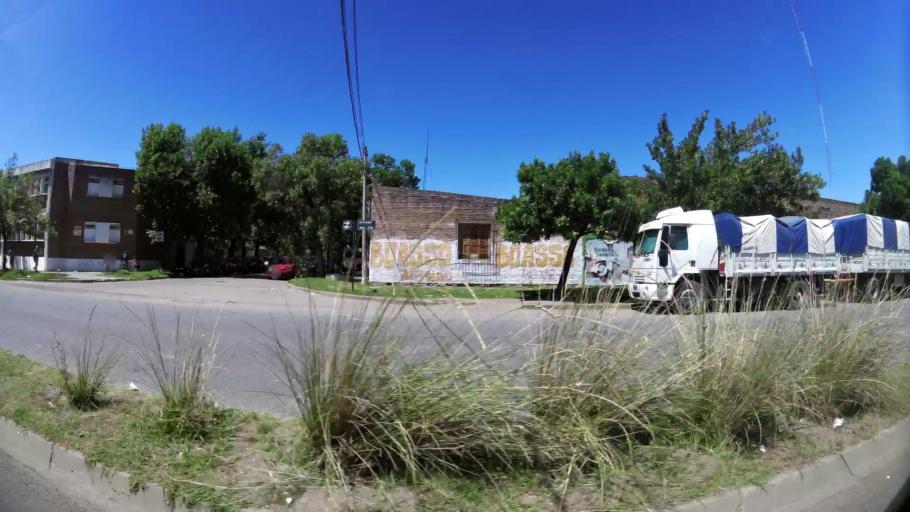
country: AR
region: Santa Fe
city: Santa Fe de la Vera Cruz
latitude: -31.6263
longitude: -60.7153
